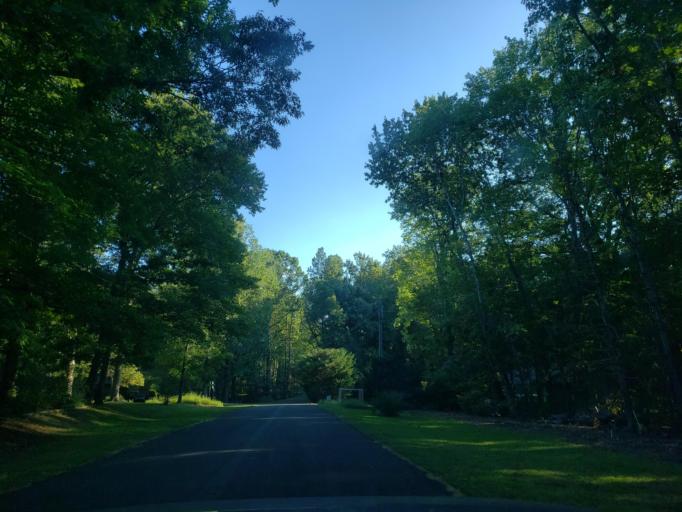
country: US
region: North Carolina
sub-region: Vance County
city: Henderson
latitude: 36.4059
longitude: -78.3809
